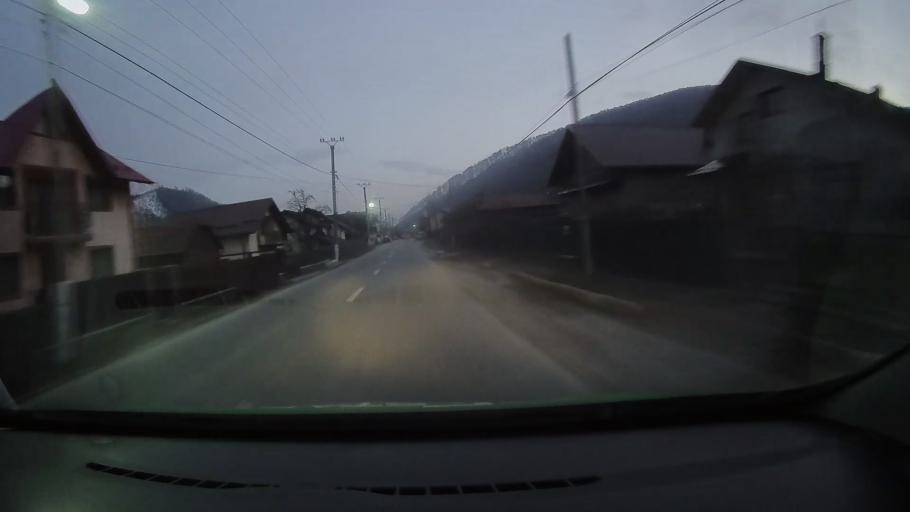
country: RO
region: Prahova
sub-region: Comuna Valea Doftanei
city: Tesila
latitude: 45.2904
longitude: 25.7227
